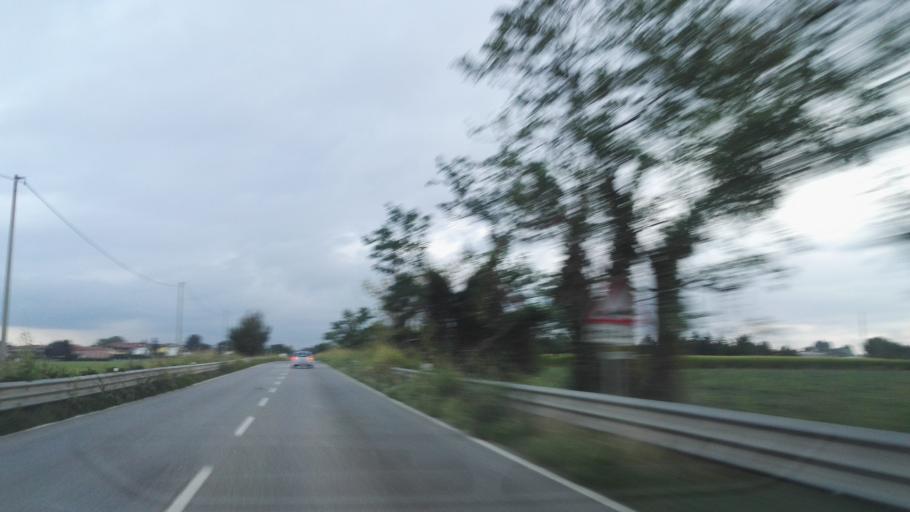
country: IT
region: Lombardy
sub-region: Citta metropolitana di Milano
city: Settala
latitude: 45.4477
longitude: 9.3915
